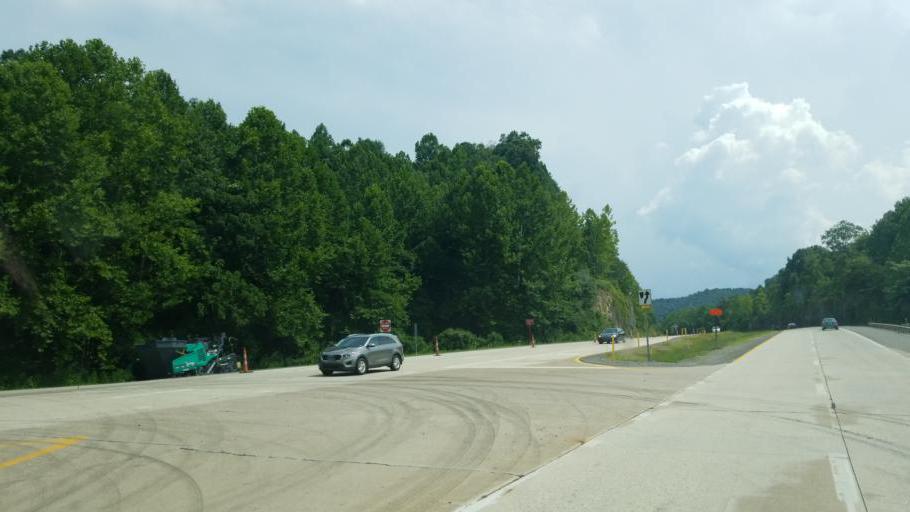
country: US
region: West Virginia
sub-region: Kanawha County
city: Alum Creek
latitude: 38.2211
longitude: -81.8346
